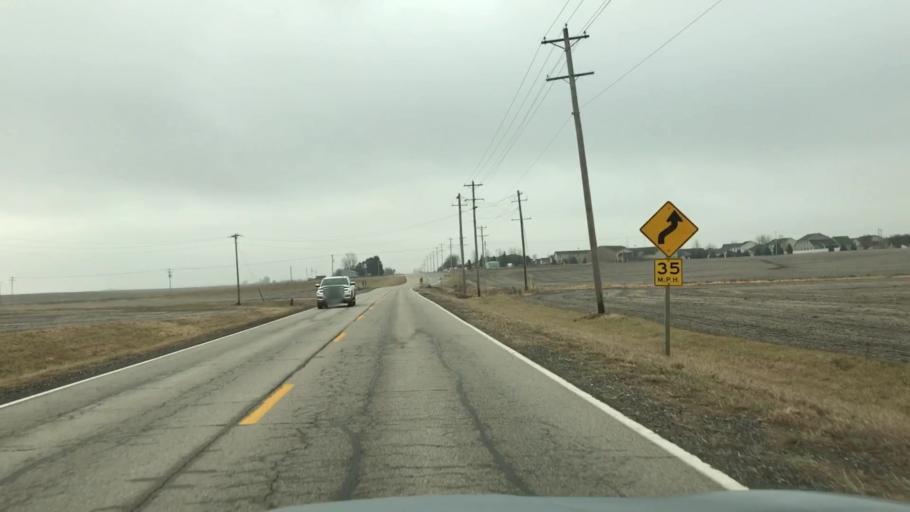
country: US
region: Illinois
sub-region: McLean County
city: Hudson
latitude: 40.5648
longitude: -88.9446
